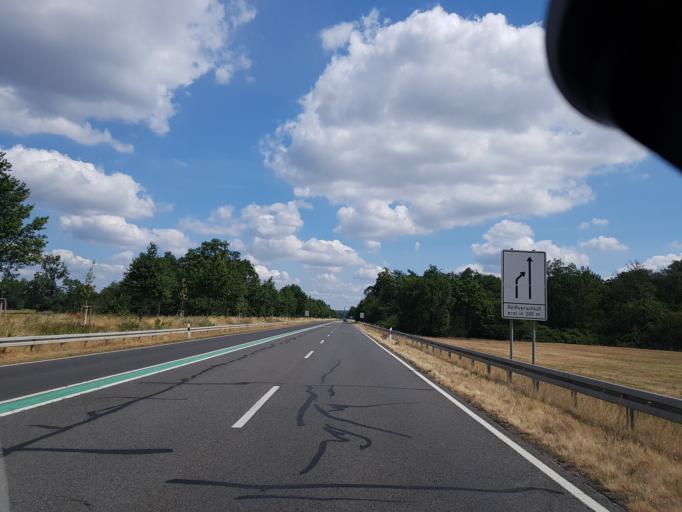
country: DE
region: Brandenburg
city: Drebkau
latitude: 51.6751
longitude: 14.2510
